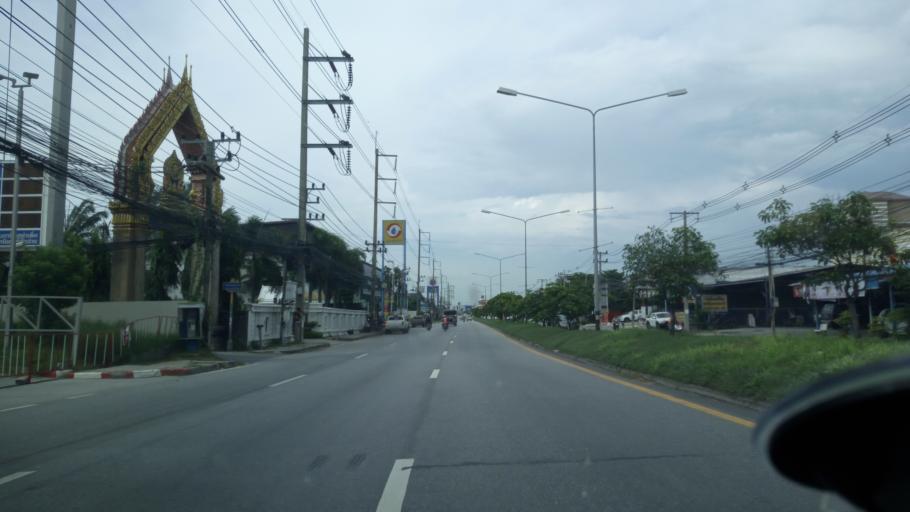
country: TH
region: Chon Buri
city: Chon Buri
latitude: 13.3901
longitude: 101.0190
